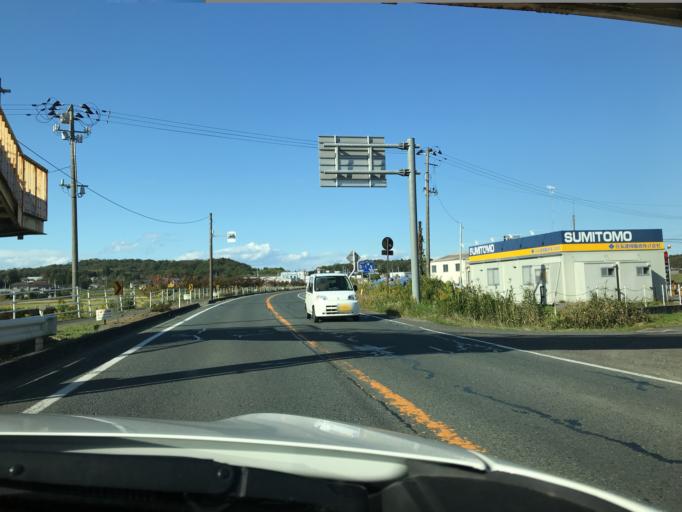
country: JP
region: Miyagi
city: Marumori
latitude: 37.7660
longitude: 140.9446
